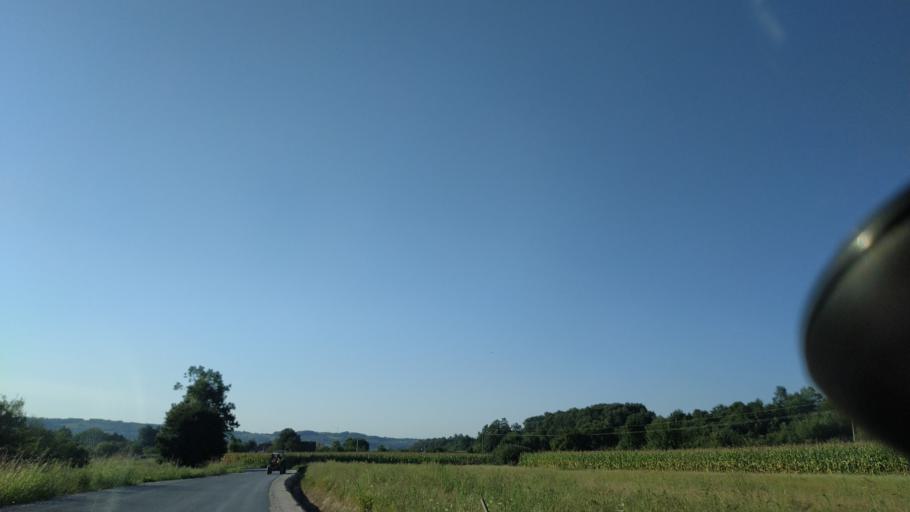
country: RS
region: Central Serbia
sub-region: Rasinski Okrug
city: Krusevac
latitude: 43.5054
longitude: 21.3353
